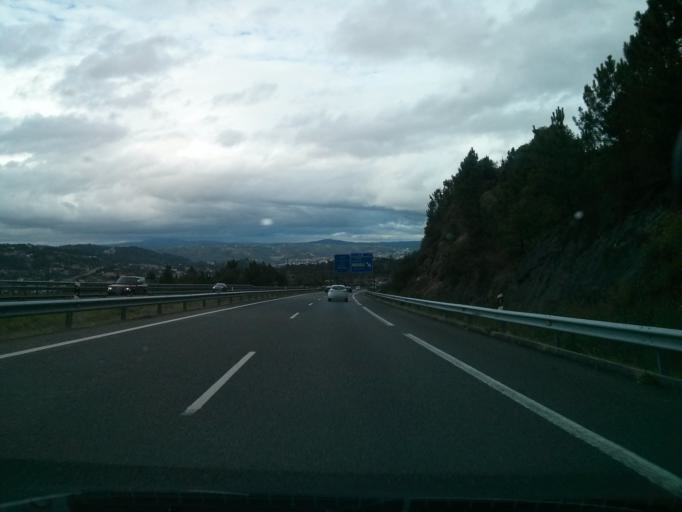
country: ES
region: Galicia
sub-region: Provincia de Ourense
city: Ourense
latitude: 42.2951
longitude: -7.8775
